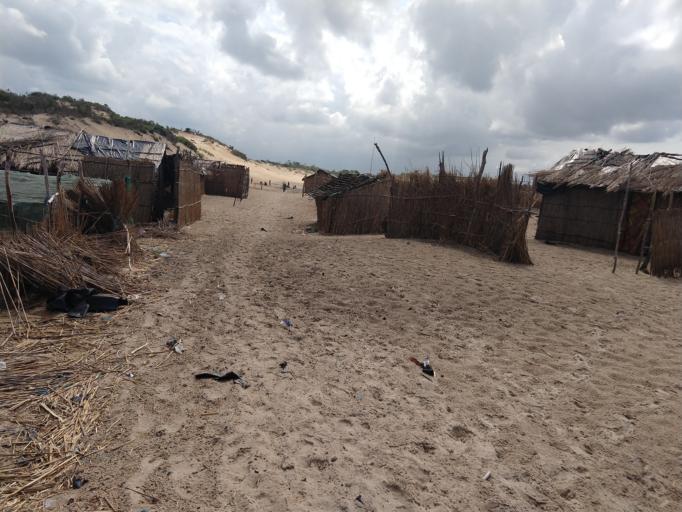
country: MZ
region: Sofala
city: Beira
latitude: -19.6483
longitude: 35.1795
